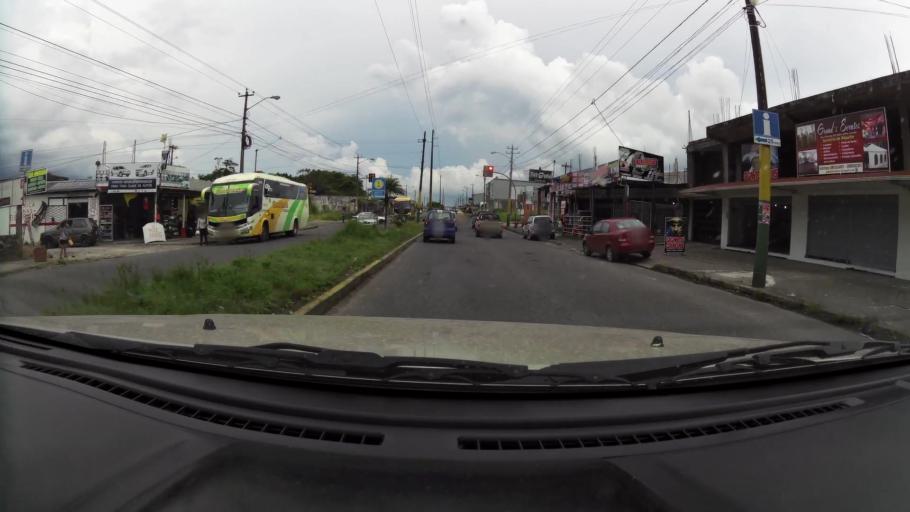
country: EC
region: Pastaza
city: Puyo
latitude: -1.4914
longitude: -78.0038
